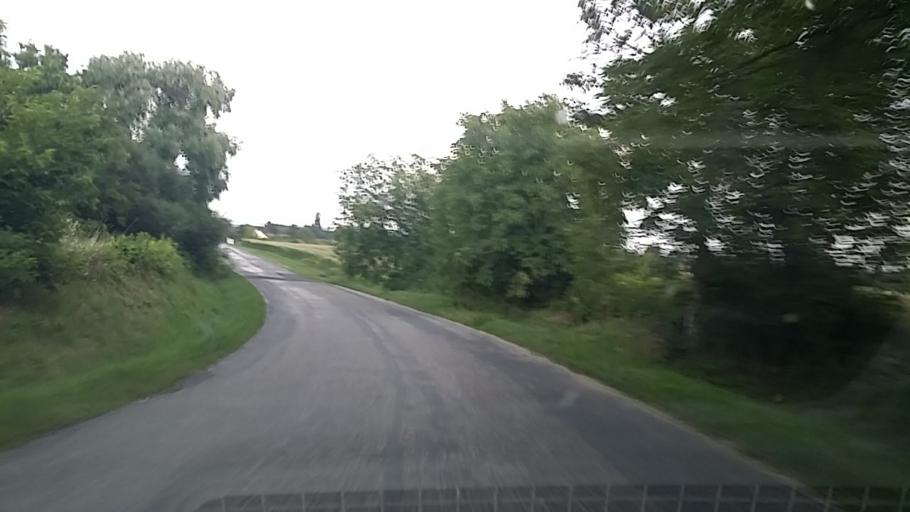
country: HU
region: Zala
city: Zalakomar
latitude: 46.5126
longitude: 17.1172
